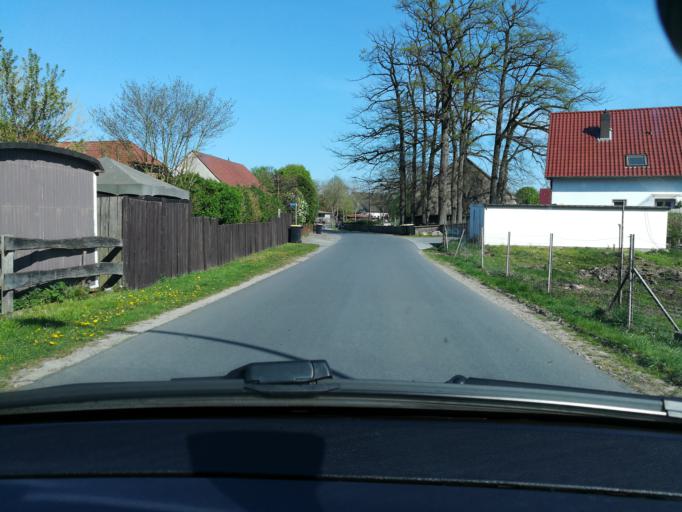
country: DE
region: North Rhine-Westphalia
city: Borgholzhausen
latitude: 52.1045
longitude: 8.3341
